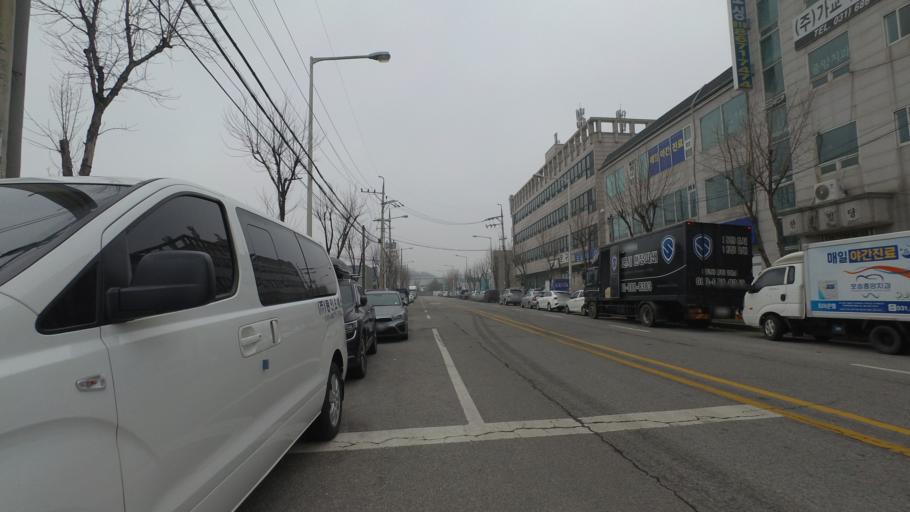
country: KR
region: Chungcheongnam-do
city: Tangjin
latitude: 36.9751
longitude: 126.8434
